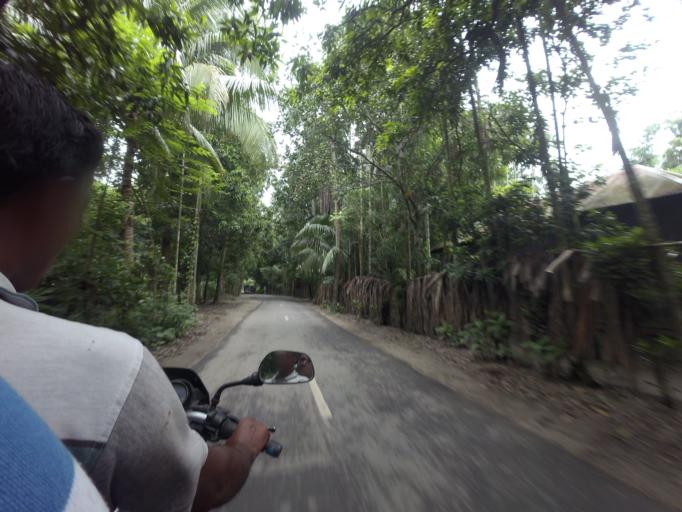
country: BD
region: Khulna
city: Kalia
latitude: 23.1293
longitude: 89.6460
